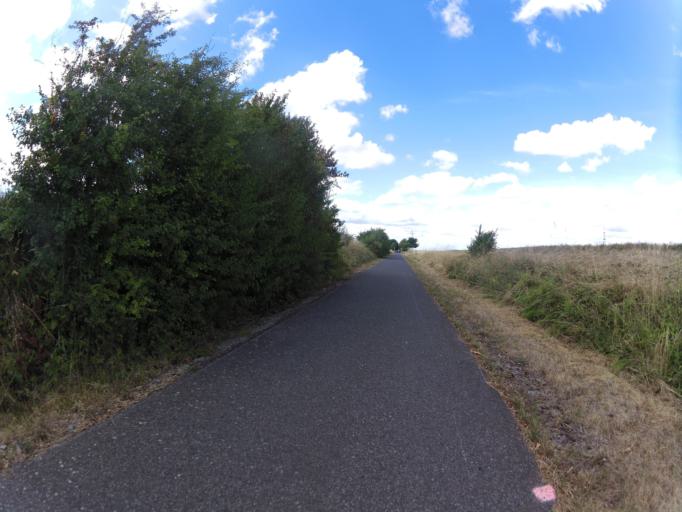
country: DE
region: Bavaria
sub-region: Regierungsbezirk Unterfranken
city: Sonderhofen
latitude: 49.5811
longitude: 10.0098
